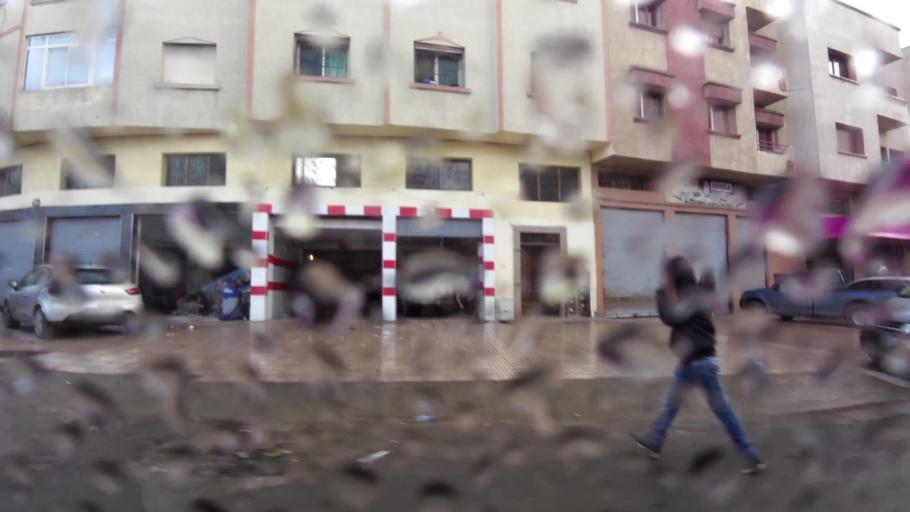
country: MA
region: Doukkala-Abda
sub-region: El-Jadida
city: El Jadida
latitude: 33.2451
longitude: -8.5241
